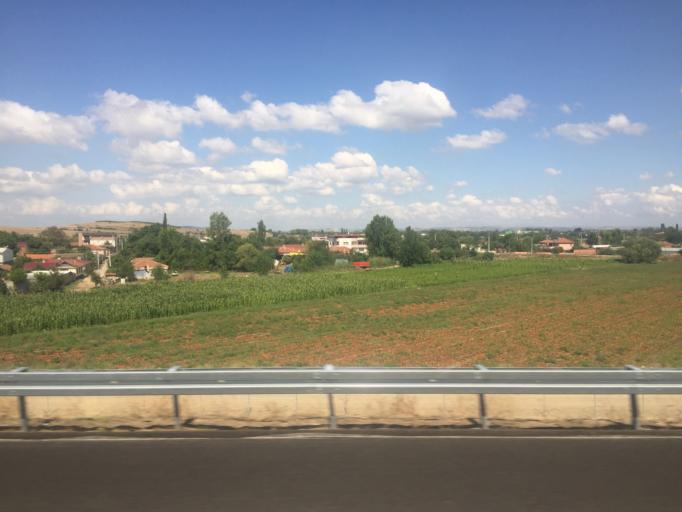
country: TR
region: Balikesir
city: Gobel
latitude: 40.0540
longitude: 28.2342
